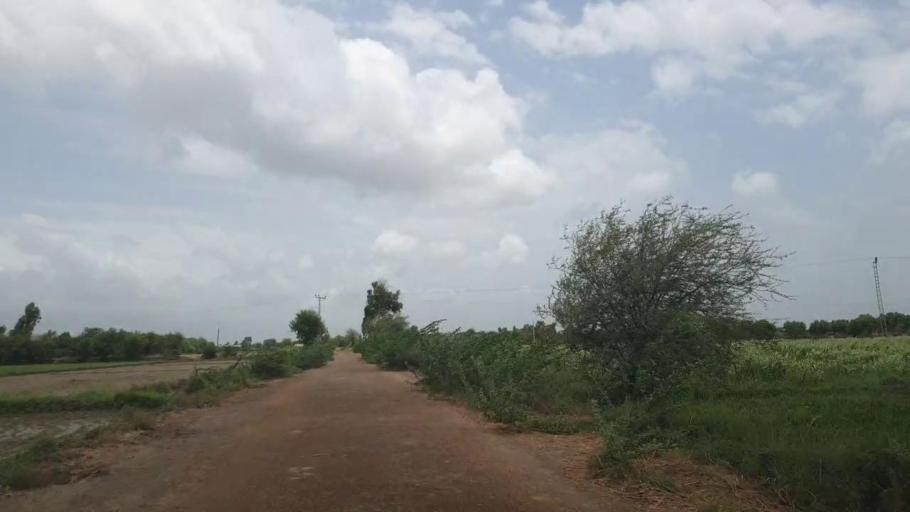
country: PK
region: Sindh
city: Badin
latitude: 24.6654
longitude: 68.8921
